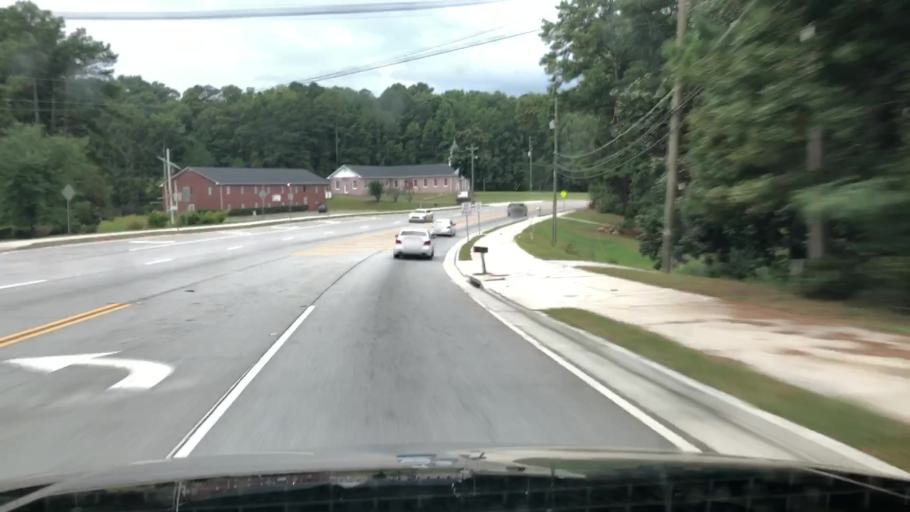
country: US
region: Georgia
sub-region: Cobb County
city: Mableton
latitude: 33.7026
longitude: -84.5645
